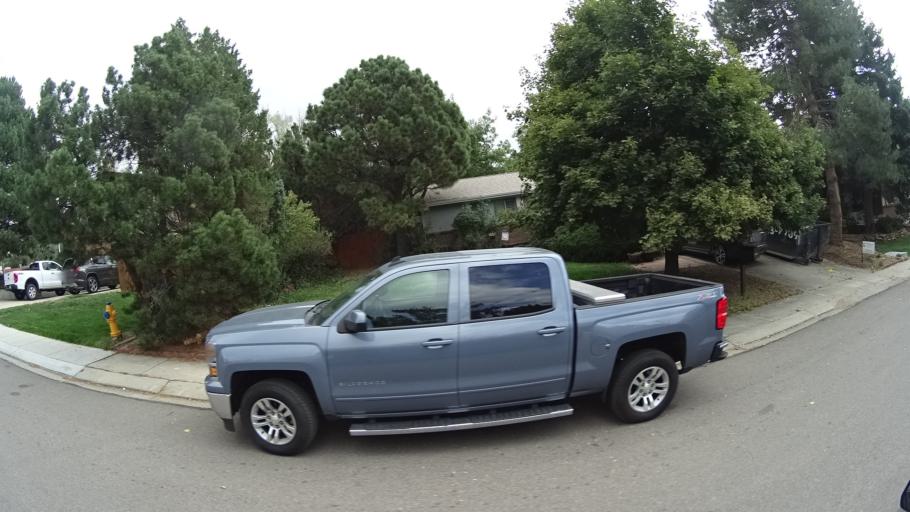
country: US
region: Colorado
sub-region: El Paso County
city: Cimarron Hills
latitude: 38.8843
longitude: -104.7319
